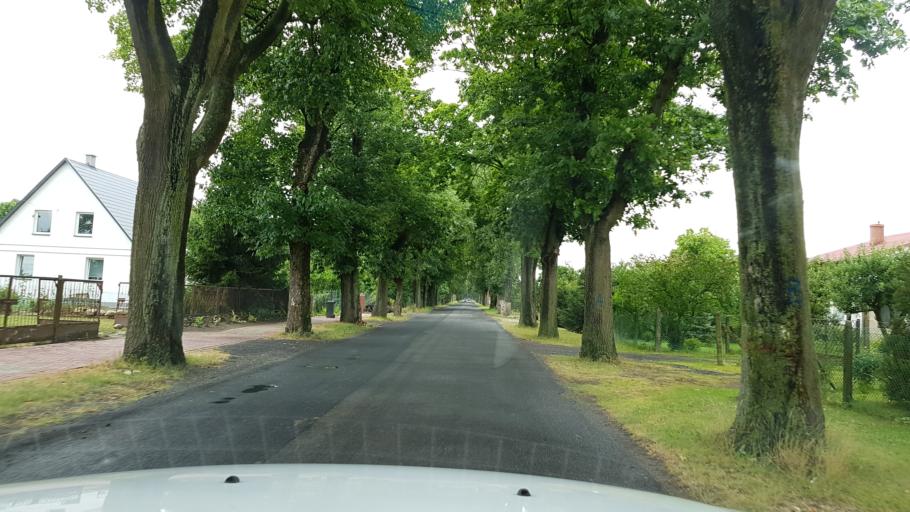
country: PL
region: West Pomeranian Voivodeship
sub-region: Powiat pyrzycki
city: Przelewice
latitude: 53.1059
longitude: 15.1406
